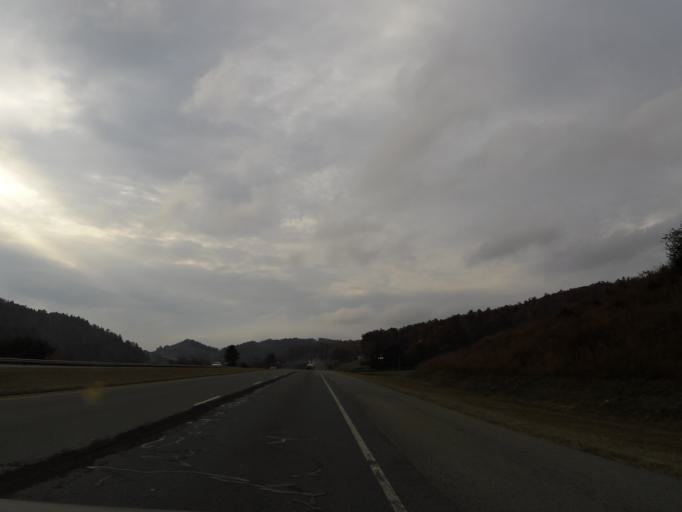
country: US
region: North Carolina
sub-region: Watauga County
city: Boone
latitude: 36.2417
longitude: -81.5254
